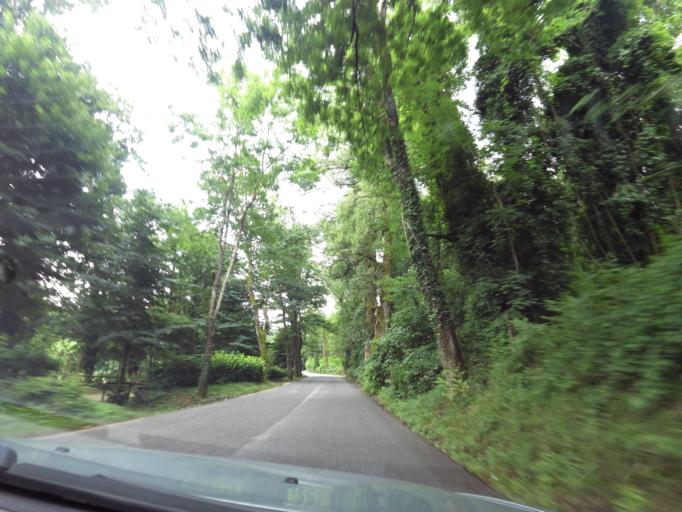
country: IT
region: Calabria
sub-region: Provincia di Vibo-Valentia
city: Serra San Bruno
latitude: 38.5636
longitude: 16.3157
